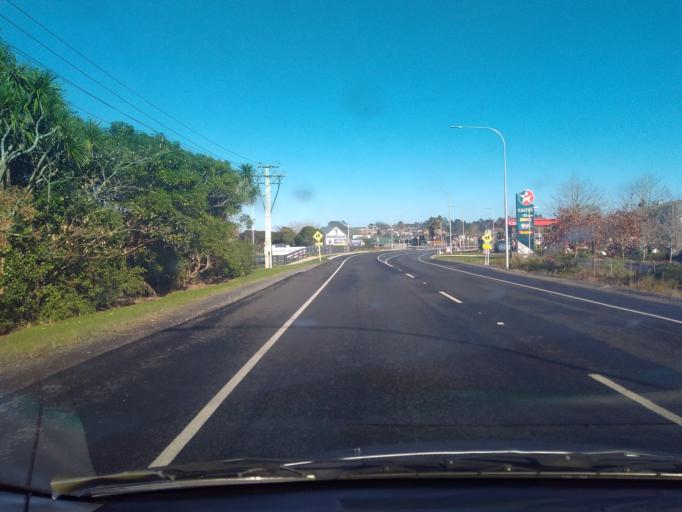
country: NZ
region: Auckland
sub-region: Auckland
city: Muriwai Beach
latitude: -36.7685
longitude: 174.4939
